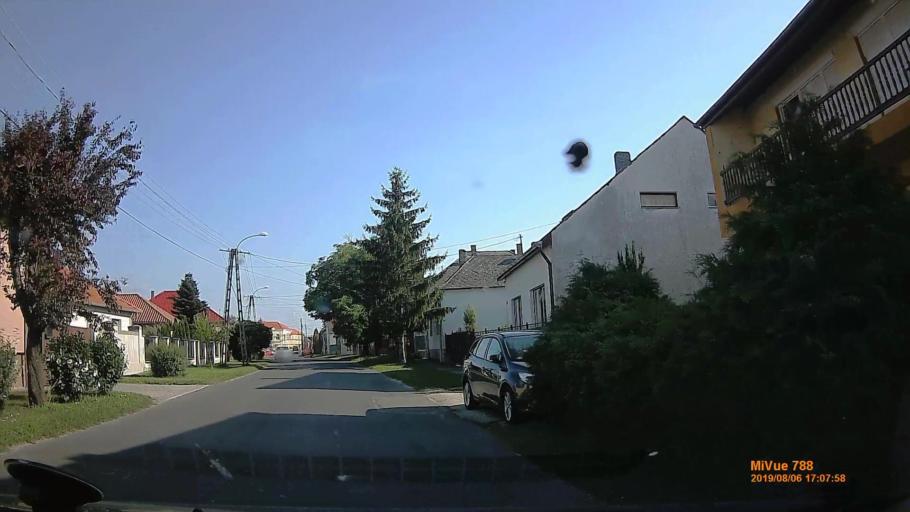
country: HU
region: Zala
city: Nagykanizsa
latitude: 46.4596
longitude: 16.9594
